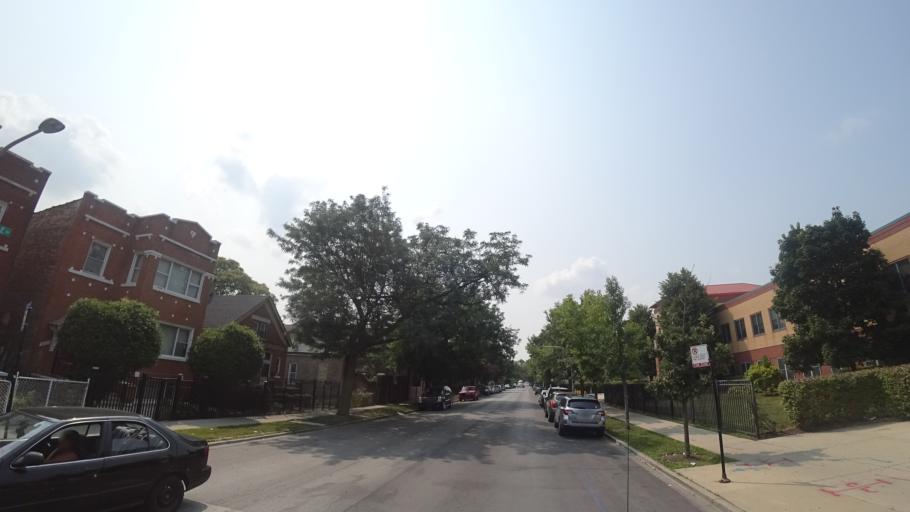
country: US
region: Illinois
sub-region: Cook County
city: Cicero
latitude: 41.8388
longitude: -87.7171
